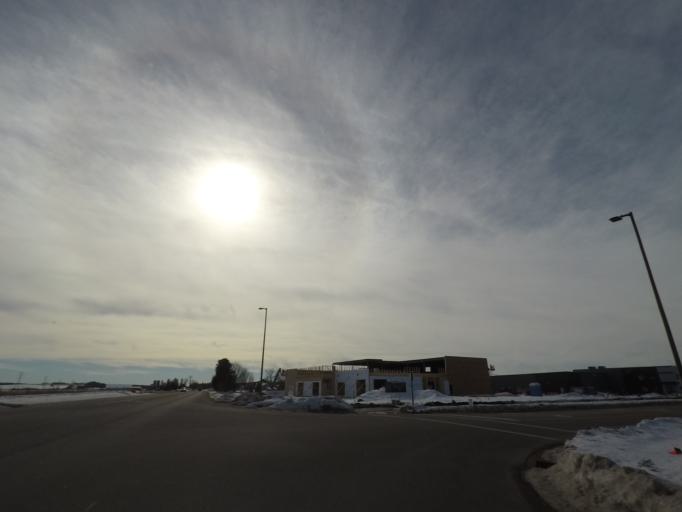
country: US
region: Wisconsin
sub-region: Dane County
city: Fitchburg
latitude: 43.0057
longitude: -89.4581
